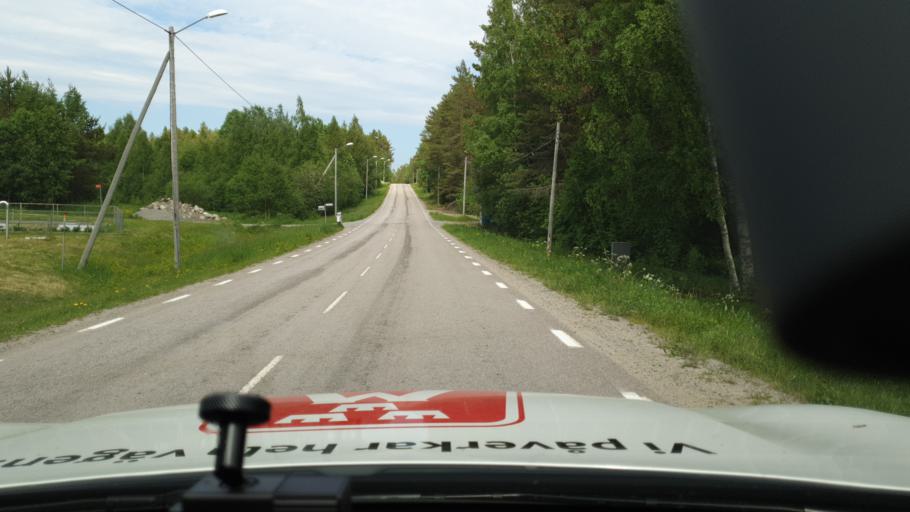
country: SE
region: Vaesterbotten
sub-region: Umea Kommun
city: Hoernefors
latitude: 63.5691
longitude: 19.8241
